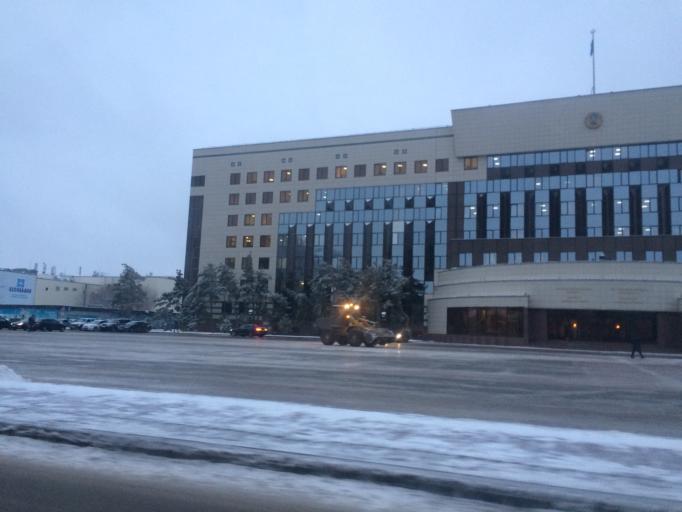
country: KZ
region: Astana Qalasy
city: Astana
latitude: 51.1670
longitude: 71.4211
